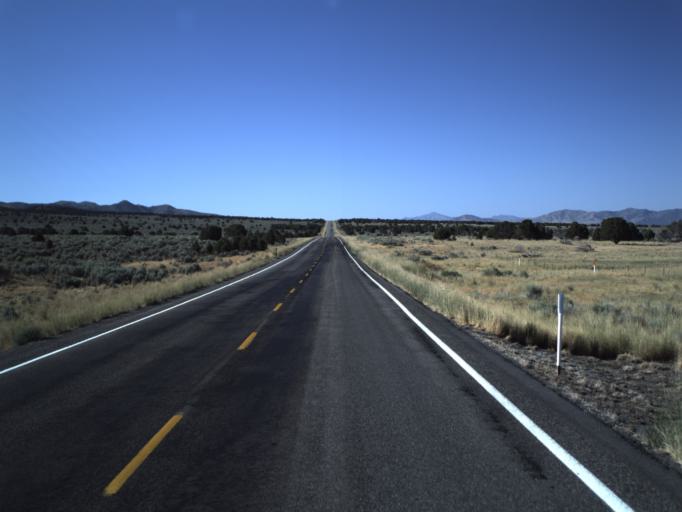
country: US
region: Utah
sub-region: Juab County
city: Mona
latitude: 39.8611
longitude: -112.1381
